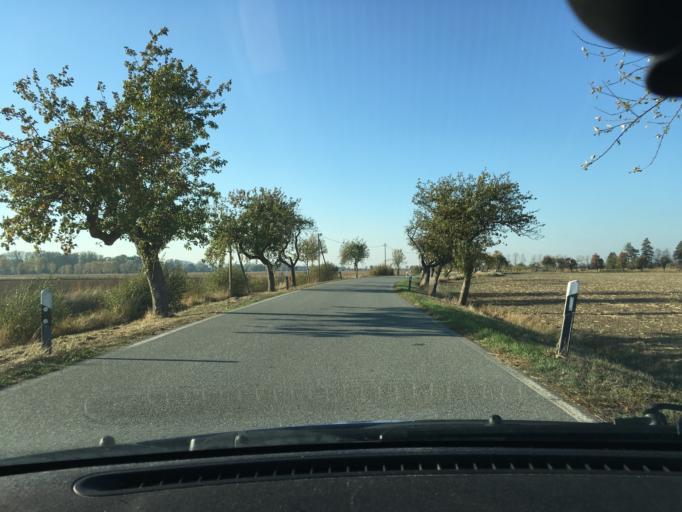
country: DE
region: Lower Saxony
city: Hitzacker
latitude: 53.1819
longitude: 11.0349
